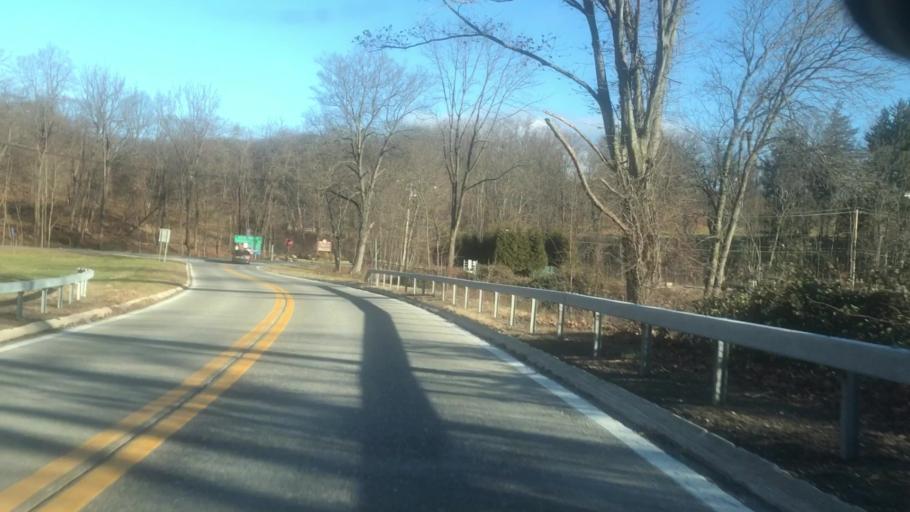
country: US
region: New York
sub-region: Rockland County
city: Thiells
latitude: 41.2173
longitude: -74.0310
